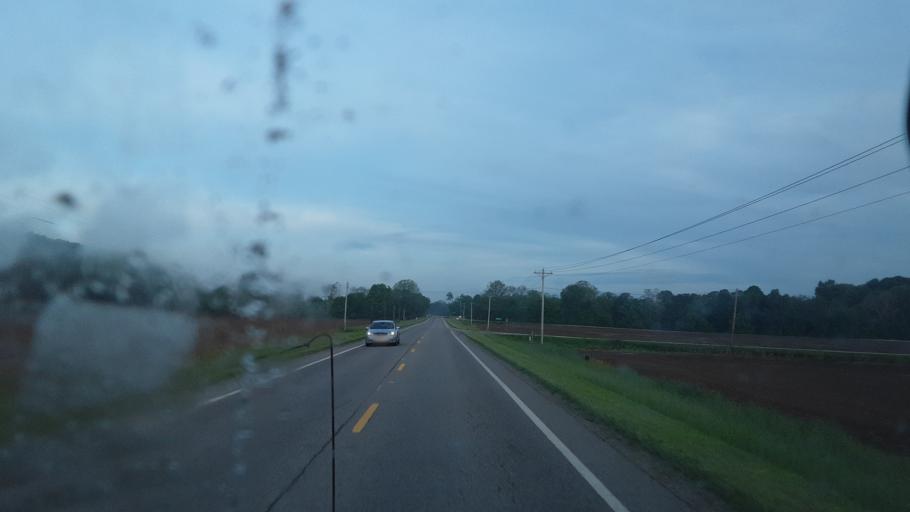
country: US
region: Ohio
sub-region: Ross County
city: Kingston
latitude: 39.4945
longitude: -82.7192
